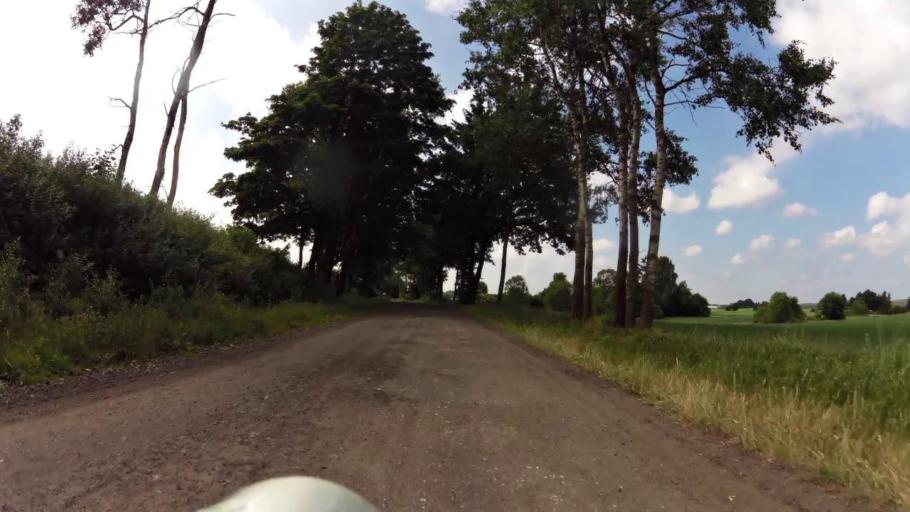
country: PL
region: West Pomeranian Voivodeship
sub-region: Powiat koszalinski
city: Bobolice
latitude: 53.9509
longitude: 16.6257
